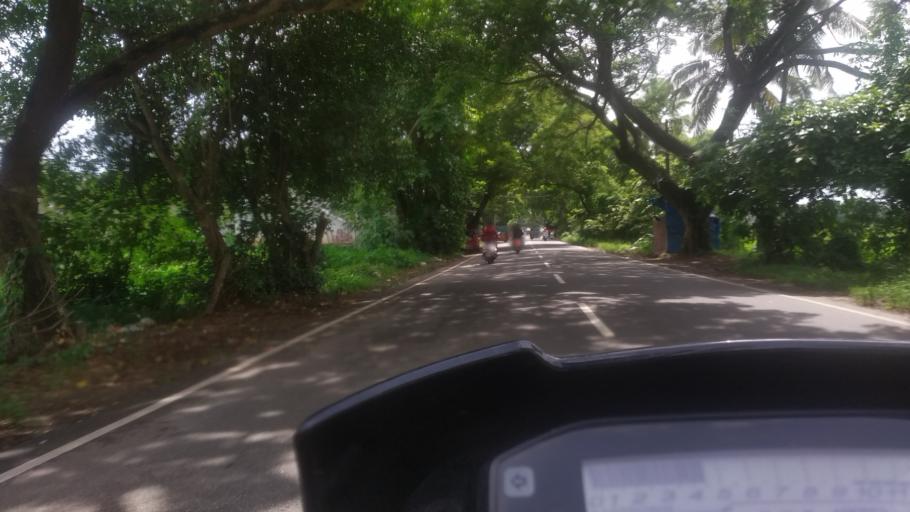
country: IN
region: Kerala
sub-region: Ernakulam
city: Elur
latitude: 10.1306
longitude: 76.2901
